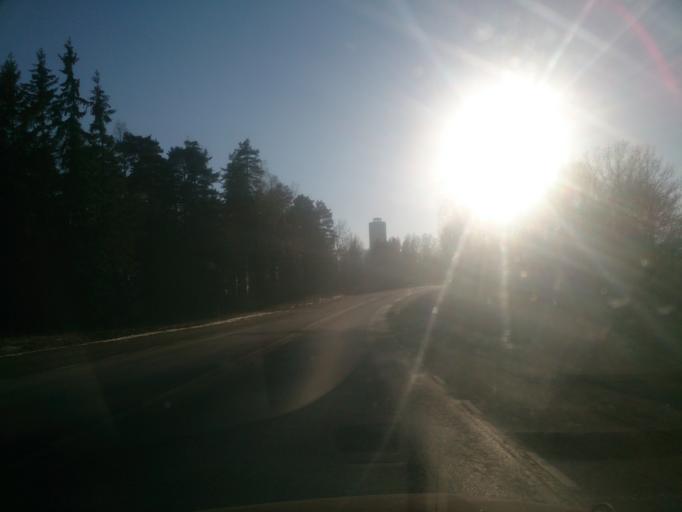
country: SE
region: OEstergoetland
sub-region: Norrkopings Kommun
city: Kimstad
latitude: 58.5046
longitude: 15.9804
